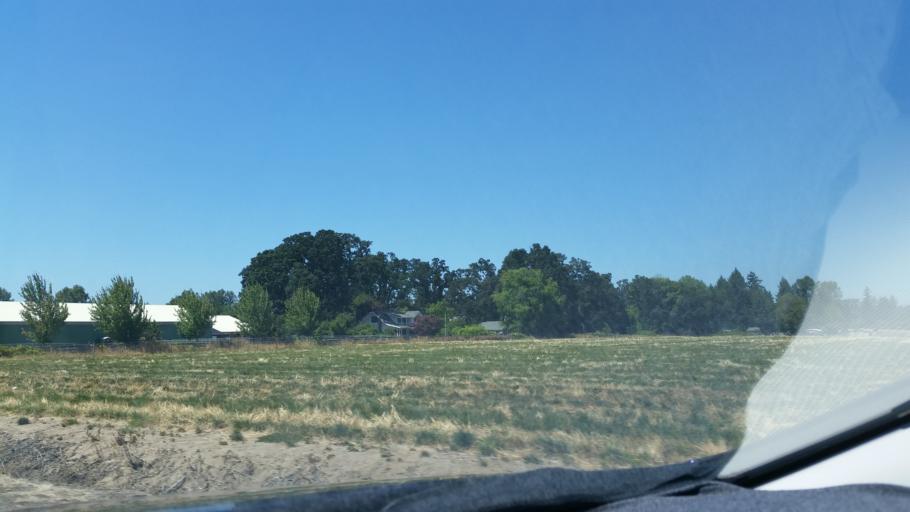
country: US
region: Oregon
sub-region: Clackamas County
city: Wilsonville
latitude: 45.2596
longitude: -122.8210
